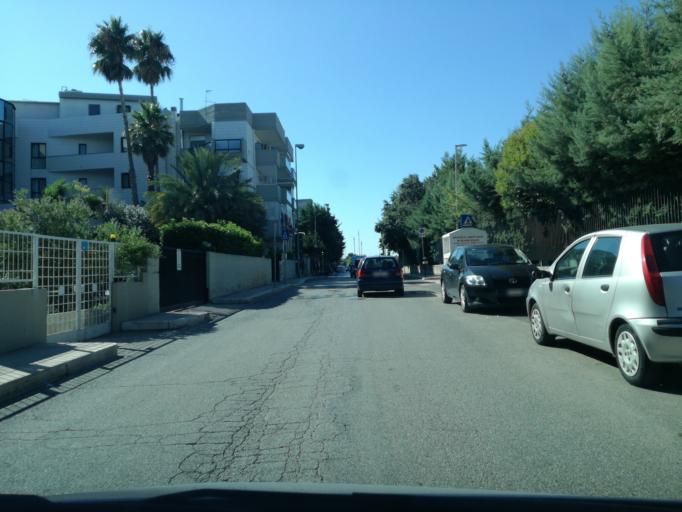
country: IT
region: Apulia
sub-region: Provincia di Bari
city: Capurso
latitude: 41.0483
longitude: 16.9152
